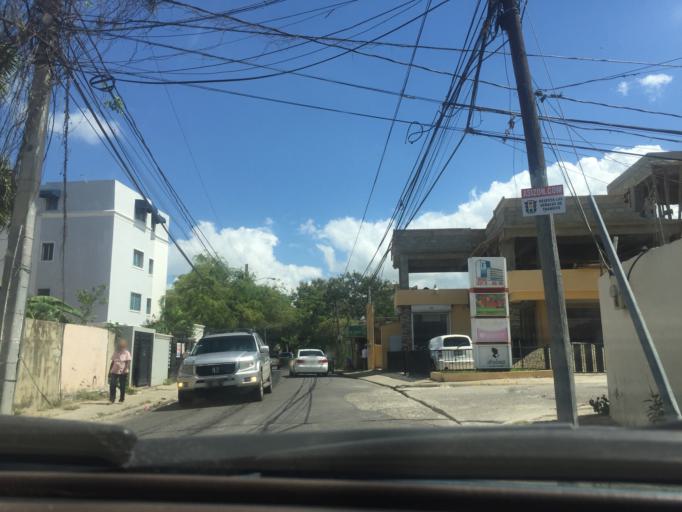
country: DO
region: Santiago
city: Santiago de los Caballeros
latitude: 19.4613
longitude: -70.6601
